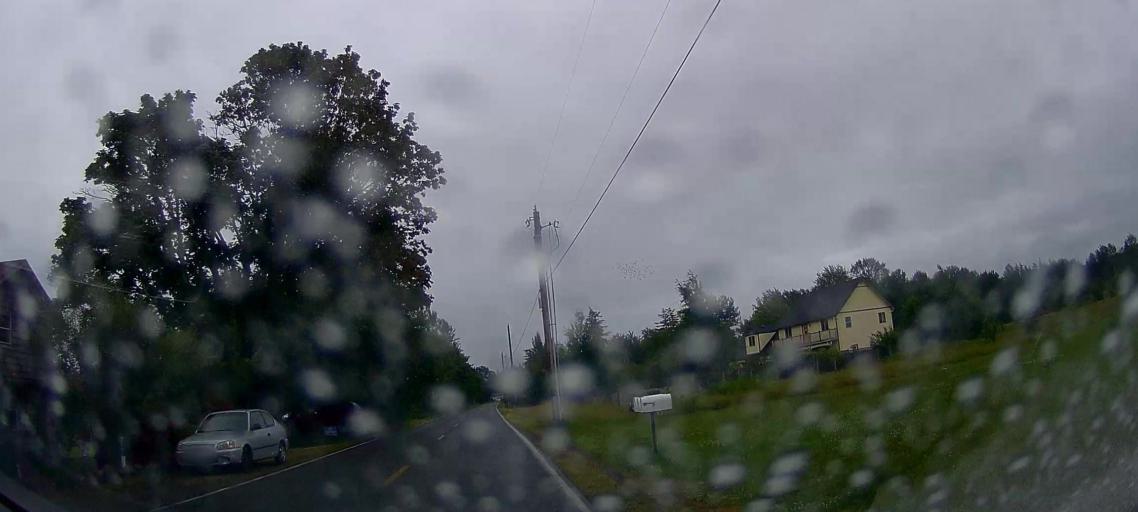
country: US
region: Washington
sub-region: Whatcom County
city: Marietta
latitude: 48.8053
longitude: -122.5716
